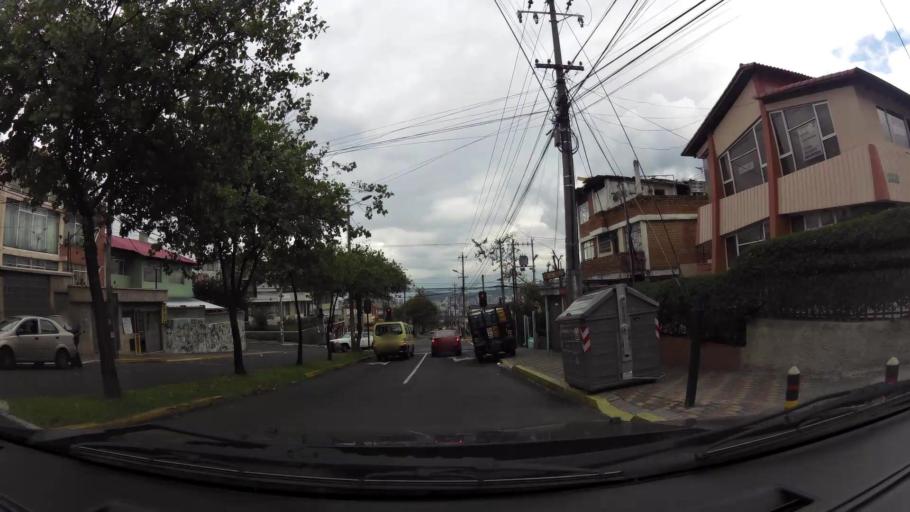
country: EC
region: Pichincha
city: Quito
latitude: -0.1945
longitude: -78.5109
